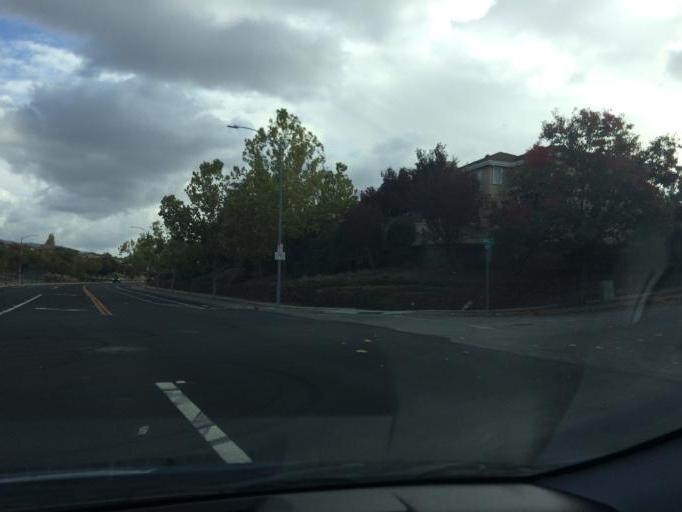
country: US
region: California
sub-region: Santa Clara County
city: Seven Trees
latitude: 37.3028
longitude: -121.7930
